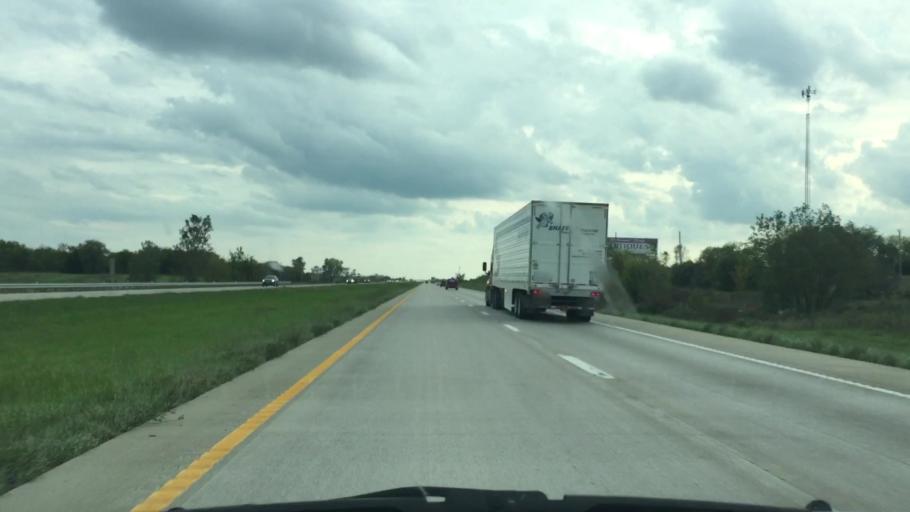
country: US
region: Missouri
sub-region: Clinton County
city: Lathrop
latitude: 39.6029
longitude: -94.2530
